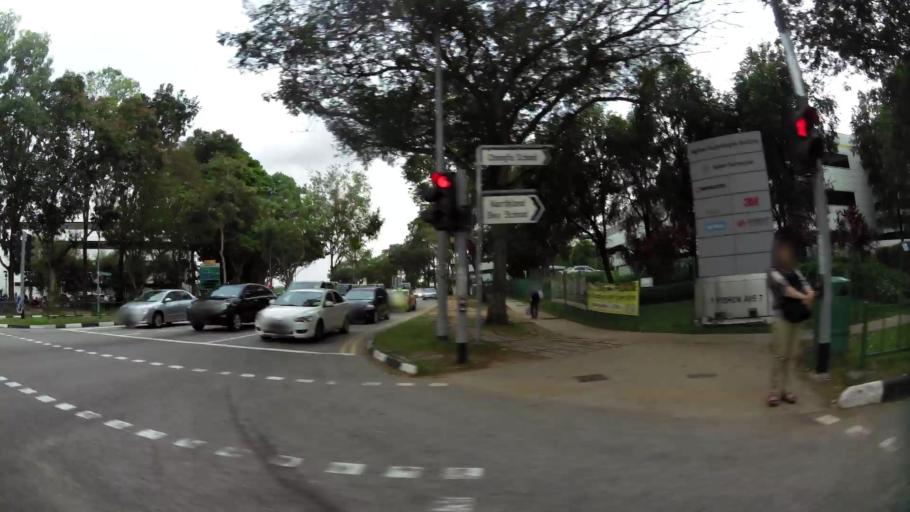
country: MY
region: Johor
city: Kampung Pasir Gudang Baru
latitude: 1.4409
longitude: 103.8394
